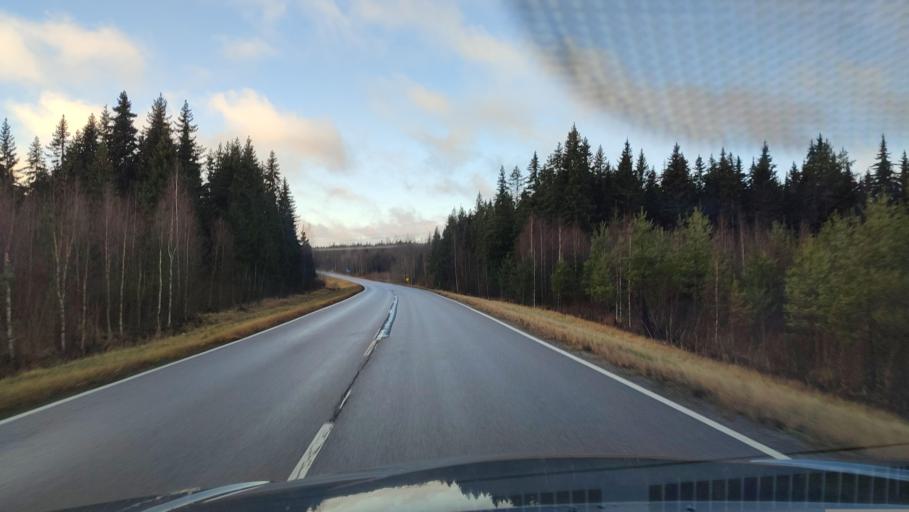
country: FI
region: Ostrobothnia
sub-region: Sydosterbotten
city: Kristinestad
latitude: 62.2989
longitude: 21.3927
